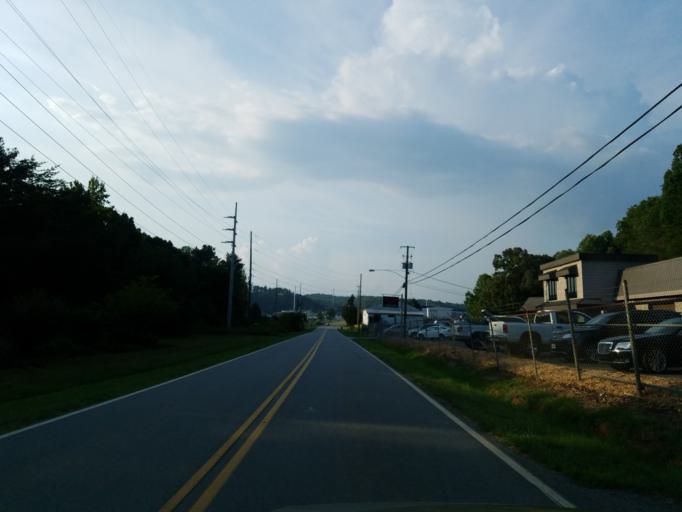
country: US
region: Georgia
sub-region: Gilmer County
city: Ellijay
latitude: 34.6772
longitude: -84.4895
